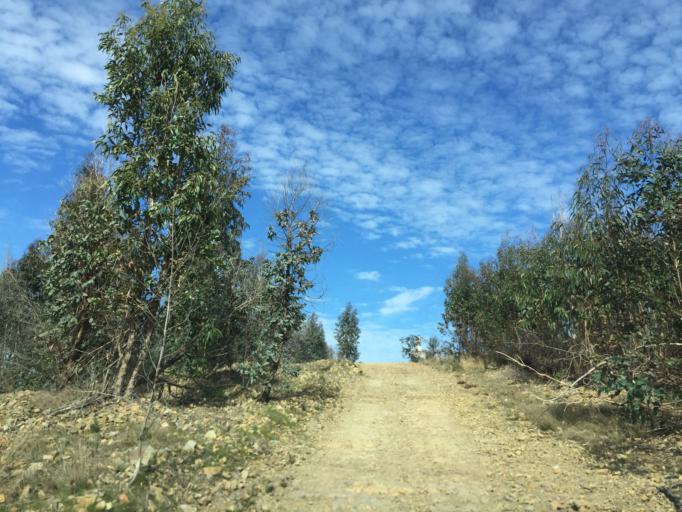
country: PT
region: Aveiro
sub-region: Arouca
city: Arouca
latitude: 40.9631
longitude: -8.2395
